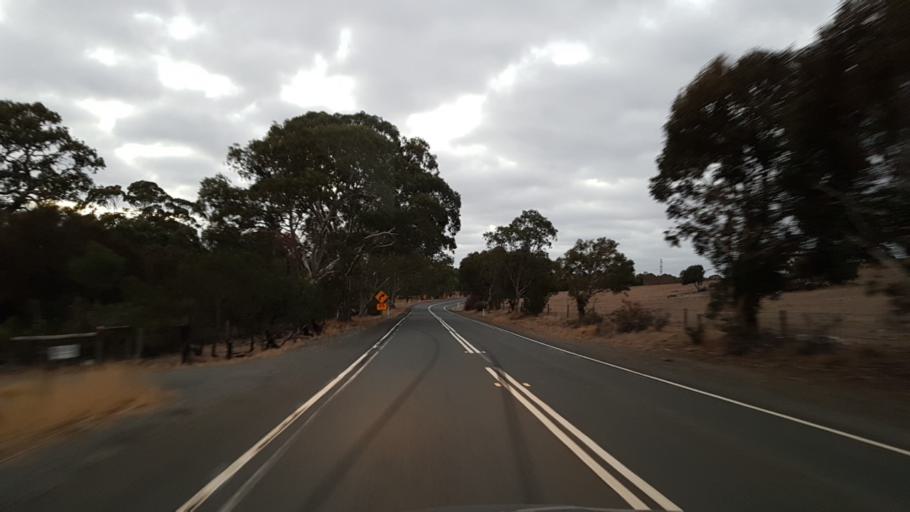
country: AU
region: South Australia
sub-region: Mount Barker
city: Nairne
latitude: -35.0423
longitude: 138.9911
